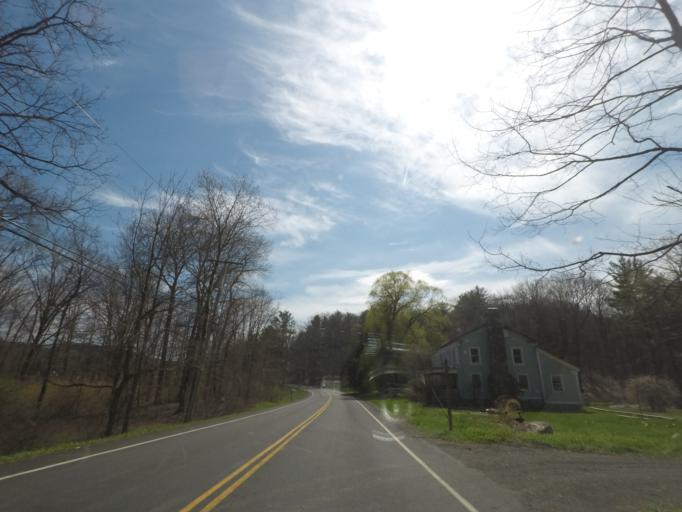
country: US
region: New York
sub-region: Columbia County
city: Chatham
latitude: 42.3901
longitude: -73.5296
